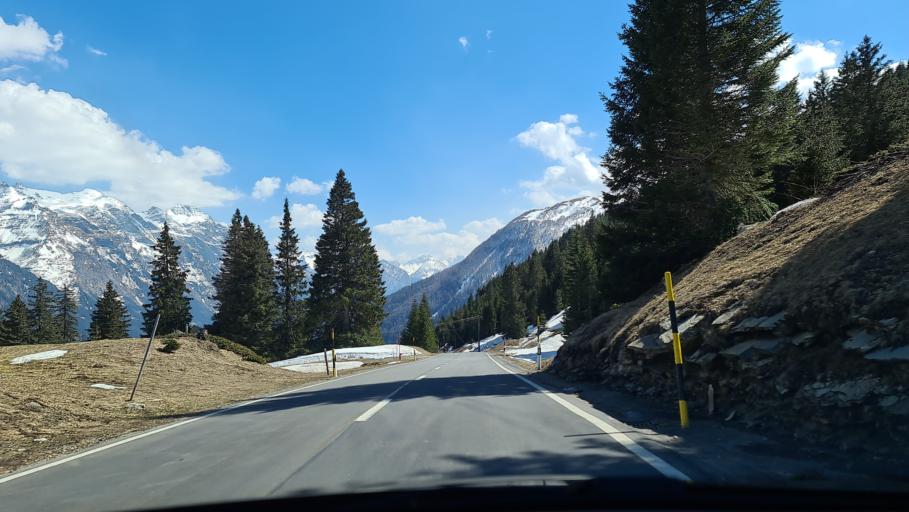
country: CH
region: Grisons
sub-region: Moesa District
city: Mesocco
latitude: 46.4460
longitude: 9.2013
